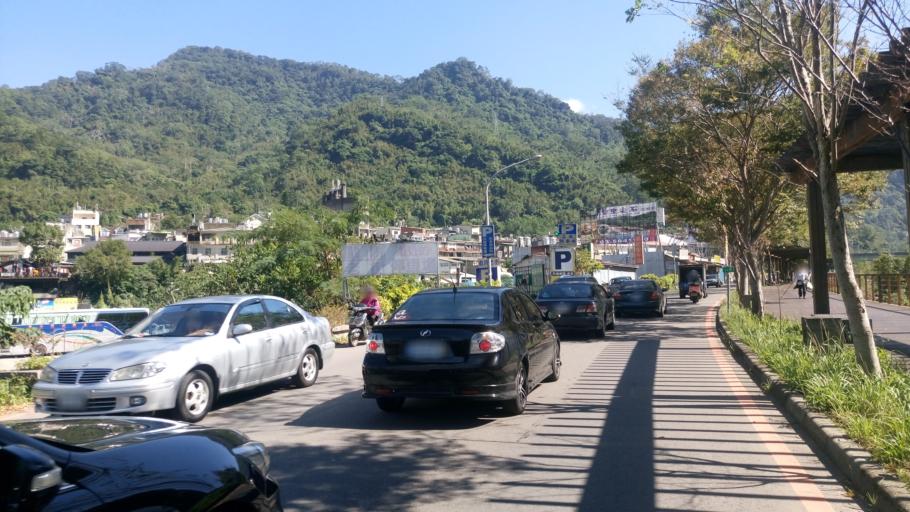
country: TW
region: Taiwan
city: Daxi
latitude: 24.7046
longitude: 121.1797
